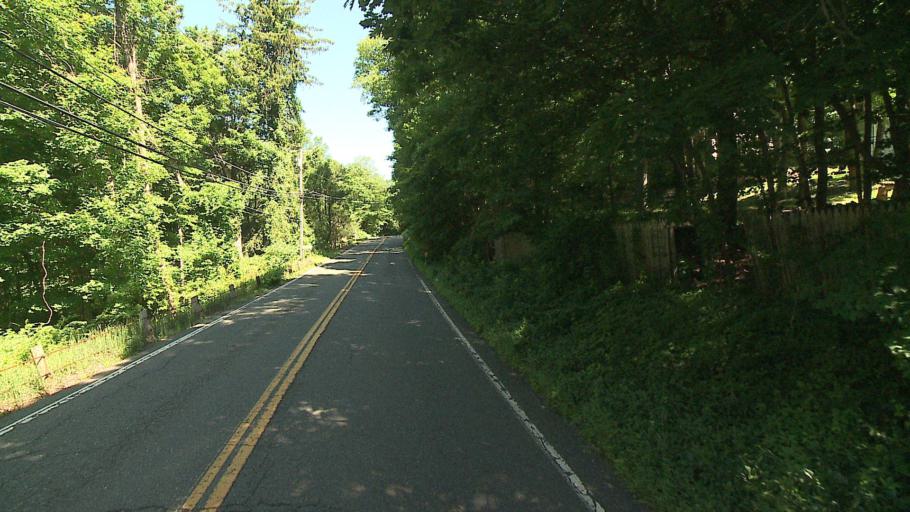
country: US
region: Connecticut
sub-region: Fairfield County
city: Ridgefield
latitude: 41.2909
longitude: -73.5249
